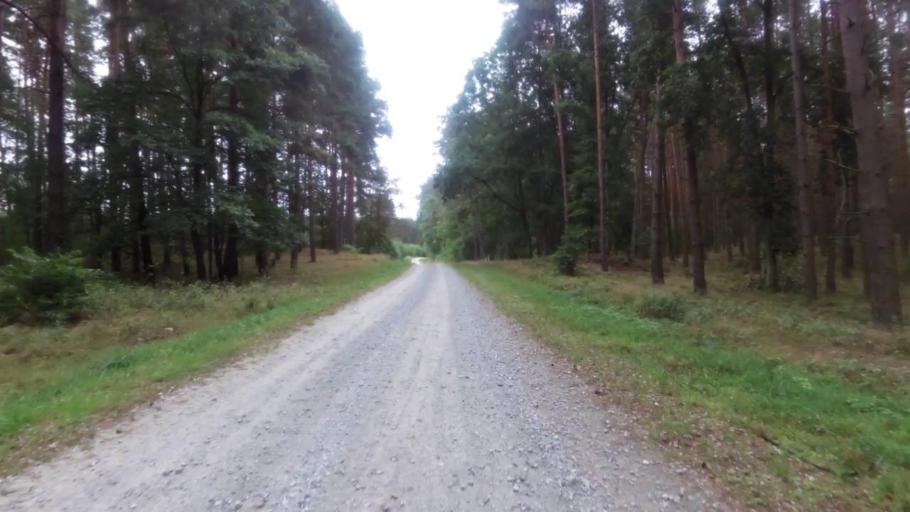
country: PL
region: Lubusz
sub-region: Powiat gorzowski
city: Kostrzyn nad Odra
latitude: 52.6477
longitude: 14.6408
